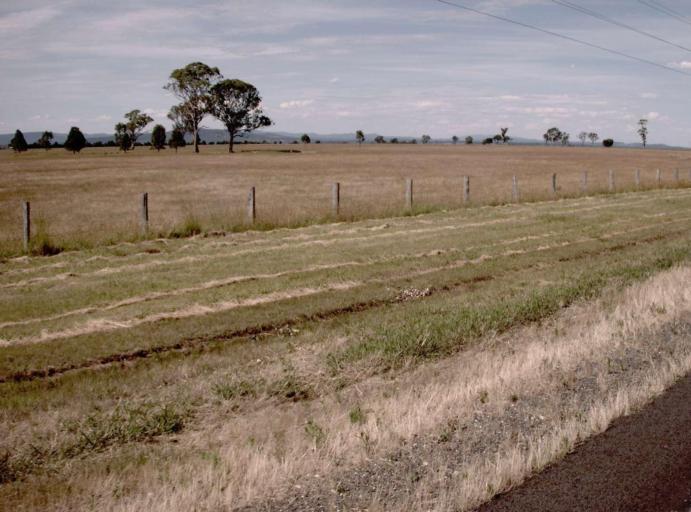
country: AU
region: Victoria
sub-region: East Gippsland
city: Bairnsdale
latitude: -37.8703
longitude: 147.4711
